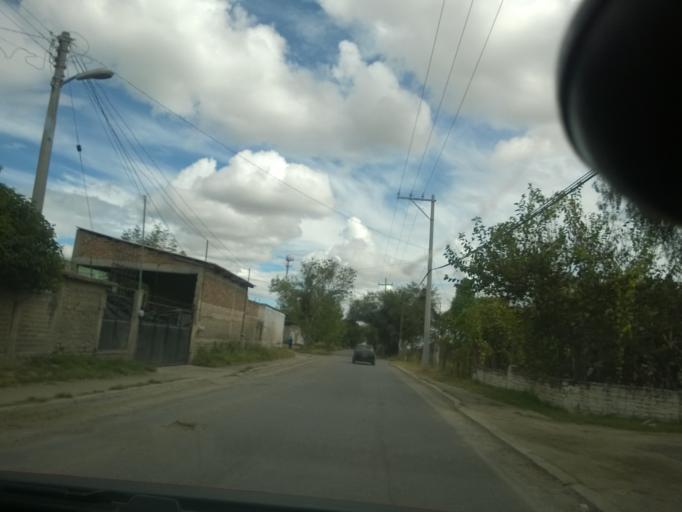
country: MX
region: Guanajuato
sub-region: Leon
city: El CERESO
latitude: 20.9976
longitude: -101.7014
